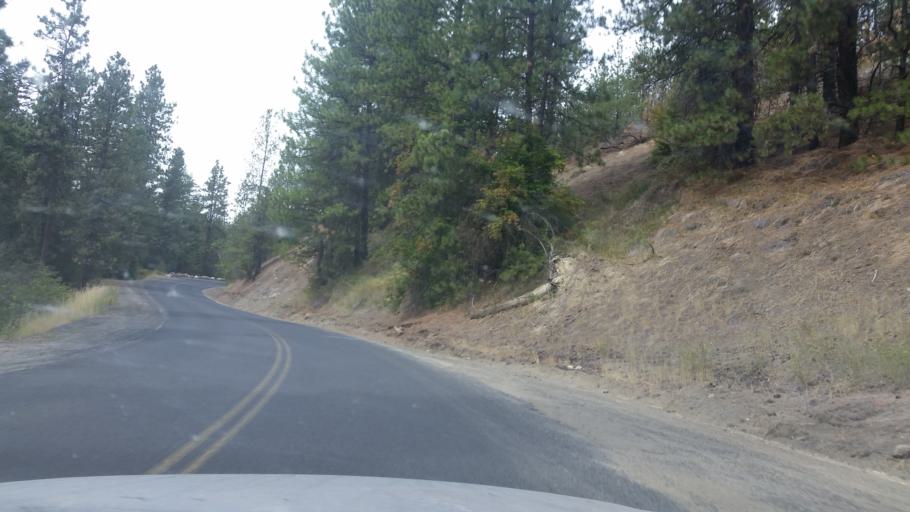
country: US
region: Washington
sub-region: Spokane County
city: Spokane
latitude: 47.6550
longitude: -117.4734
